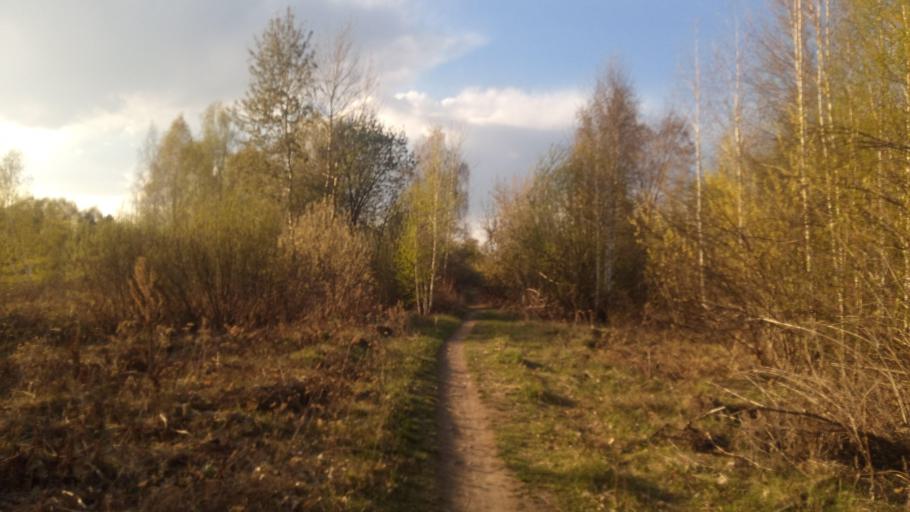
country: RU
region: Chelyabinsk
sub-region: Gorod Chelyabinsk
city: Chelyabinsk
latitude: 55.1500
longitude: 61.3245
